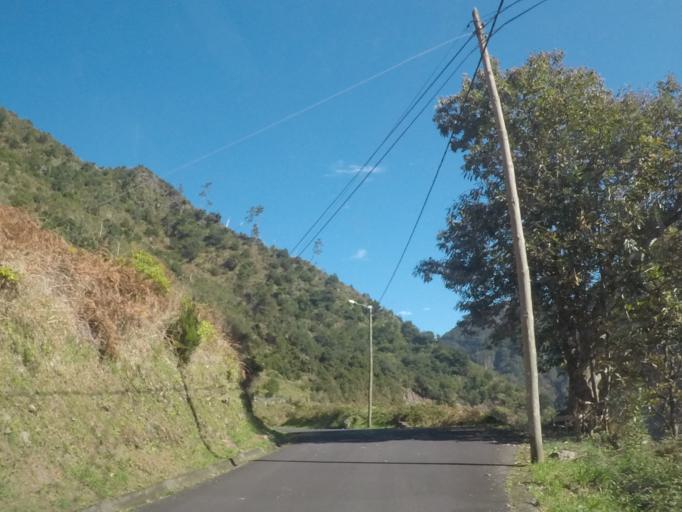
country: PT
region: Madeira
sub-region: Camara de Lobos
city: Curral das Freiras
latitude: 32.7834
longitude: -16.9781
